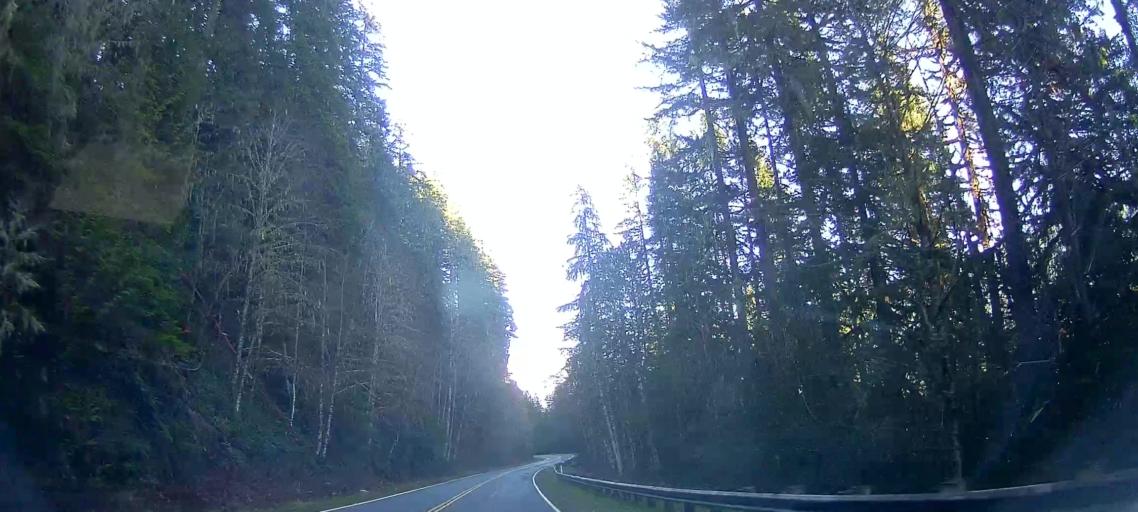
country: US
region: Washington
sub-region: Snohomish County
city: Darrington
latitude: 48.6507
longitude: -121.7116
